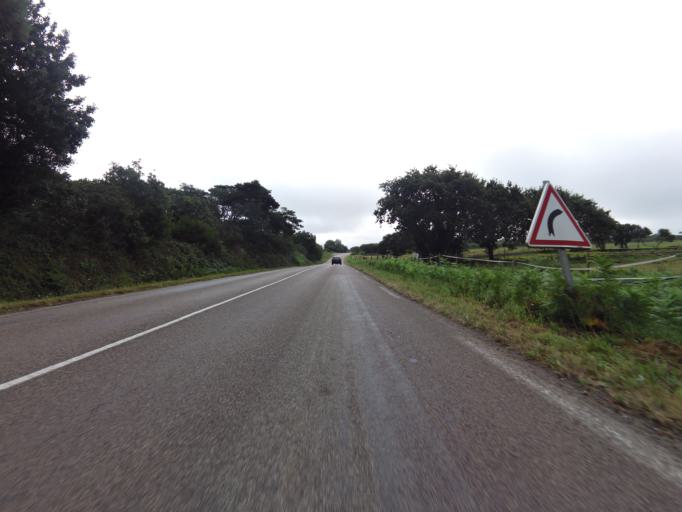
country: FR
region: Brittany
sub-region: Departement du Finistere
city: Plouhinec
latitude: 48.0120
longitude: -4.4686
